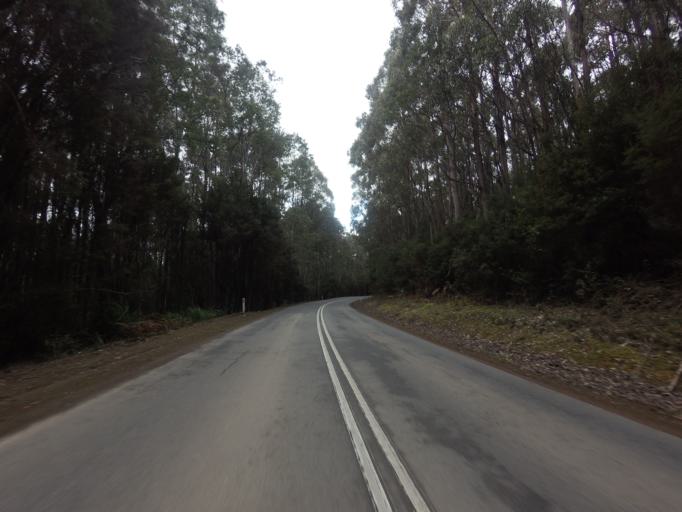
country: AU
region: Tasmania
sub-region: Huon Valley
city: Geeveston
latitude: -43.3936
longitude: 146.9567
